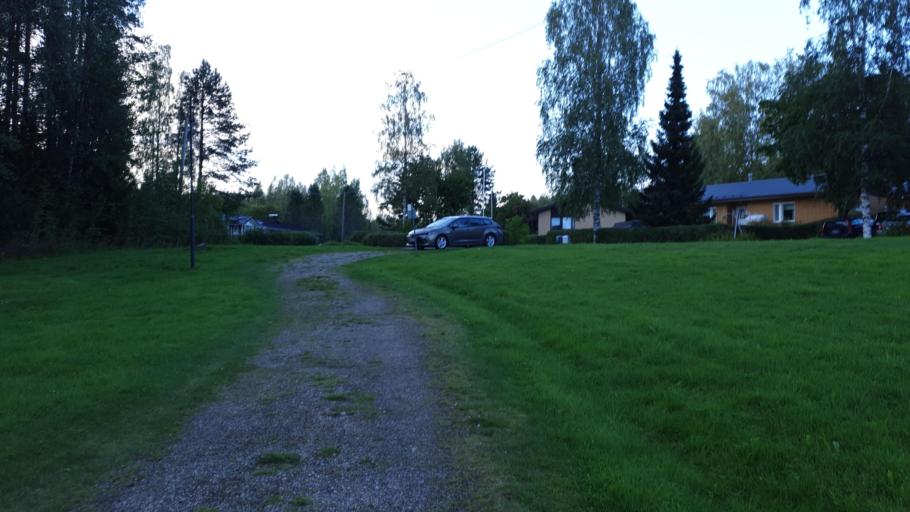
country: FI
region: Northern Savo
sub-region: Koillis-Savo
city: Kaavi
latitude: 62.9746
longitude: 28.4682
